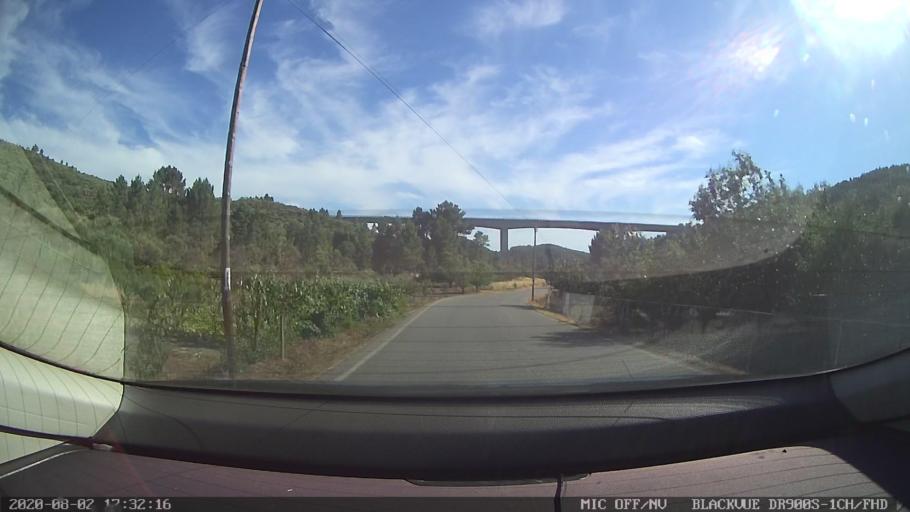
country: PT
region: Vila Real
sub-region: Sabrosa
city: Sabrosa
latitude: 41.3630
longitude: -7.5712
